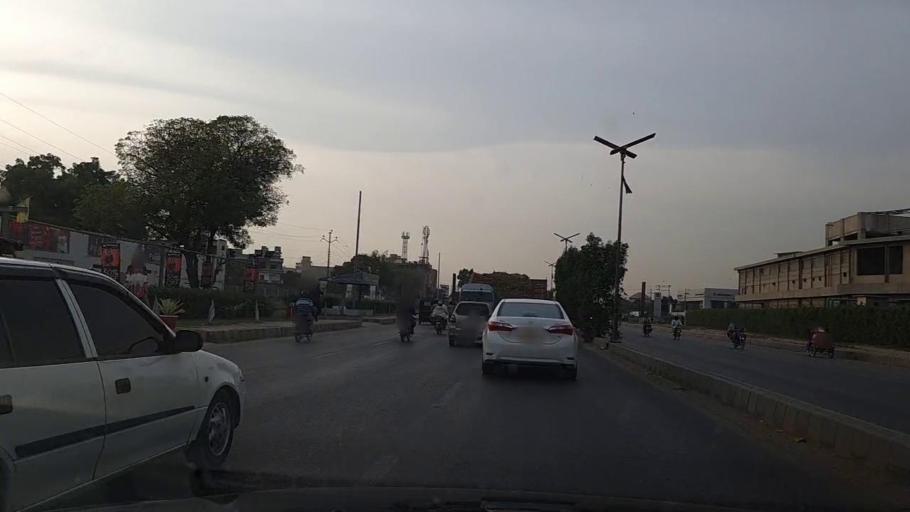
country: PK
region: Sindh
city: Malir Cantonment
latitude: 24.8534
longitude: 67.2465
